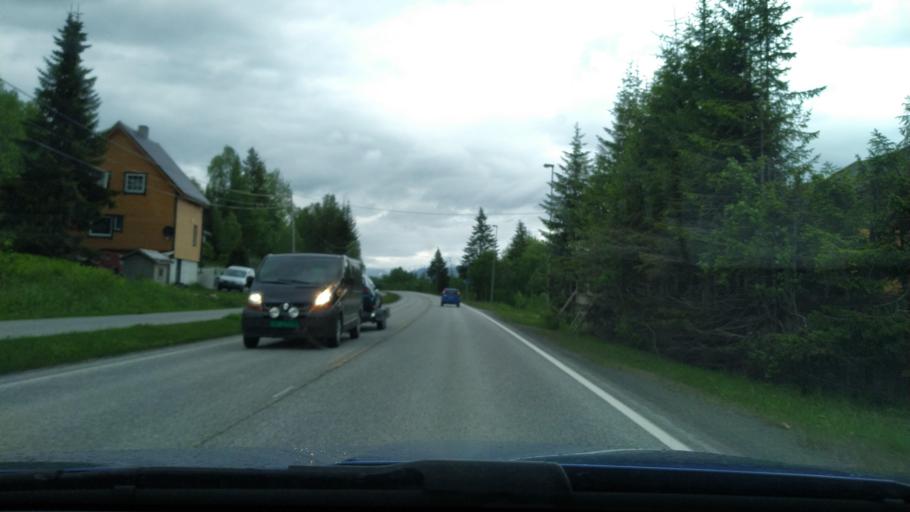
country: NO
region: Troms
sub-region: Malselv
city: Moen
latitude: 69.0245
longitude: 18.4952
